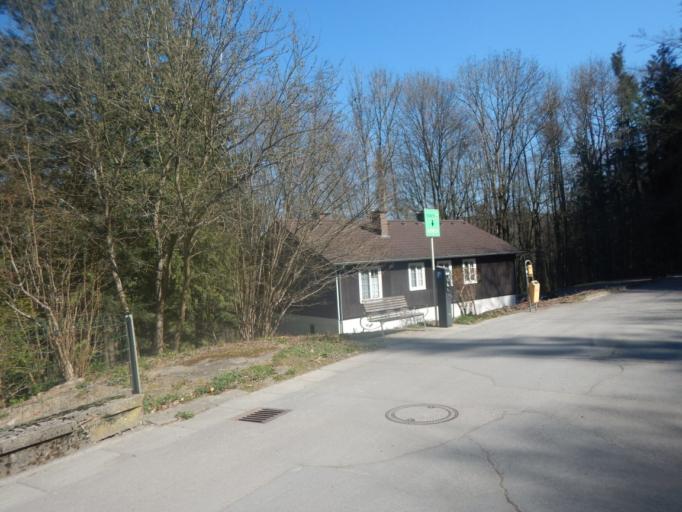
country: LU
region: Diekirch
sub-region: Canton de Wiltz
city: Wiltz
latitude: 49.9644
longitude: 5.9382
